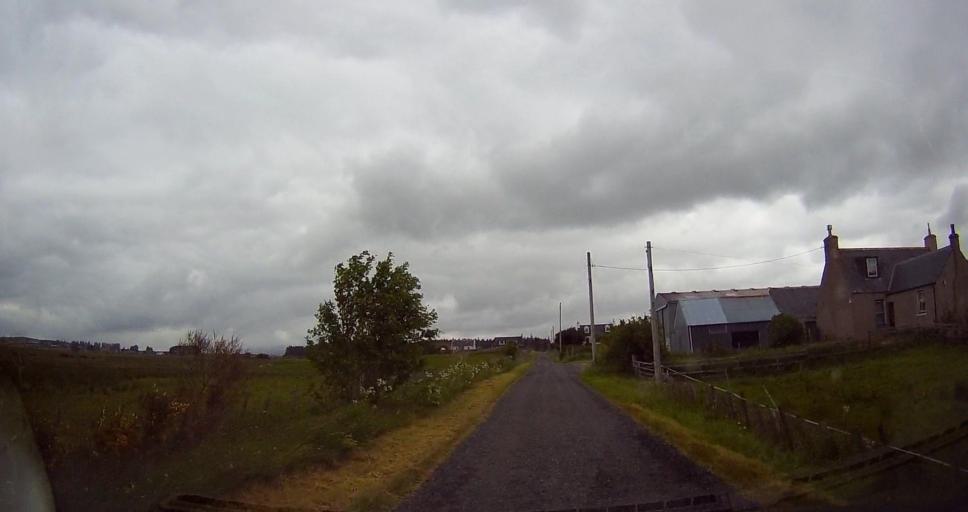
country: GB
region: Scotland
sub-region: Highland
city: Alness
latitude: 58.0611
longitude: -4.4292
